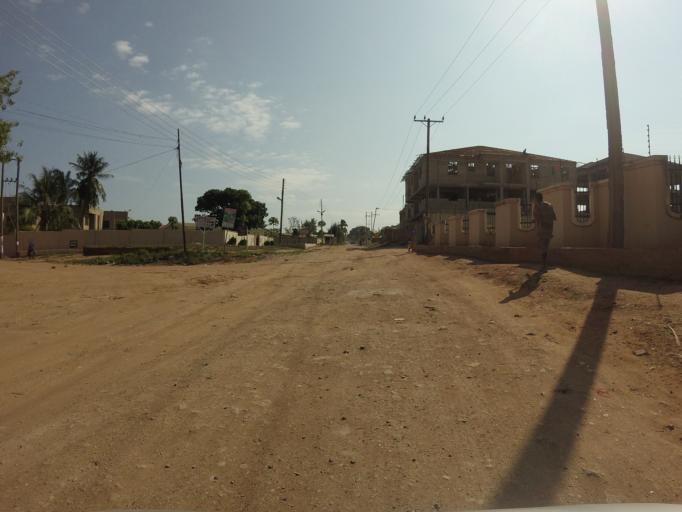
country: GH
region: Greater Accra
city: Dome
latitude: 5.6400
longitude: -0.2346
